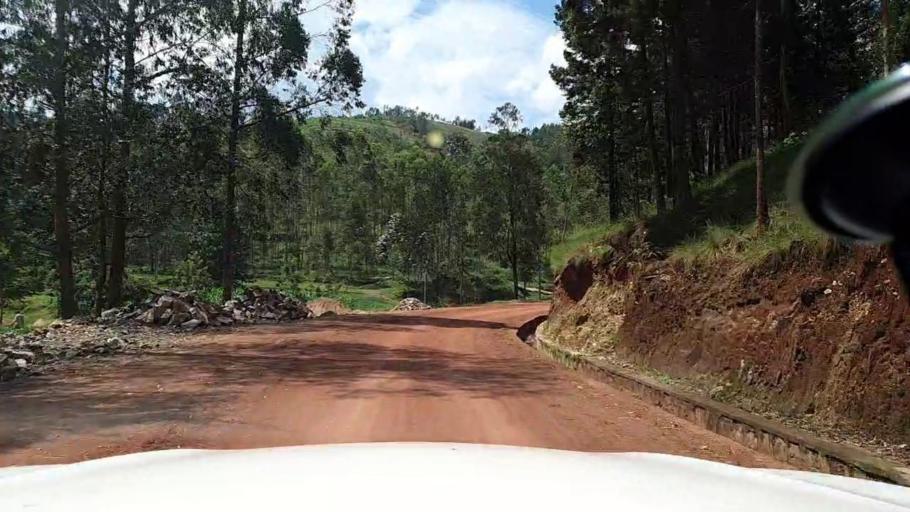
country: RW
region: Northern Province
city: Byumba
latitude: -1.7002
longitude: 29.8327
